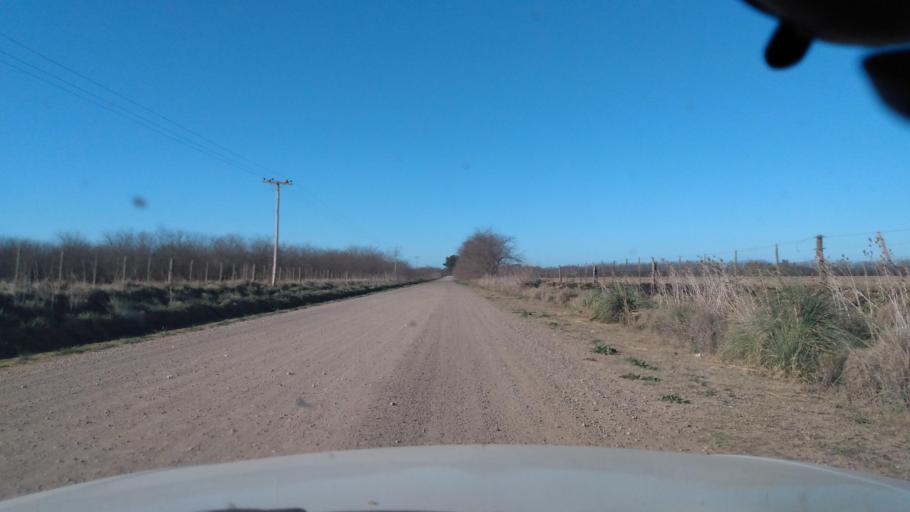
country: AR
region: Buenos Aires
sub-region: Partido de Mercedes
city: Mercedes
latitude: -34.6156
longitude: -59.3327
